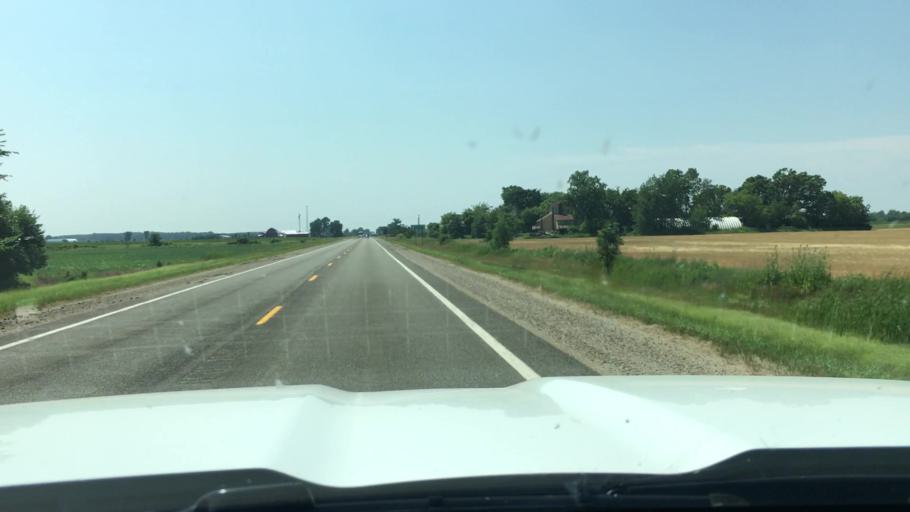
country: US
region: Michigan
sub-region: Gratiot County
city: Ithaca
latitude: 43.1759
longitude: -84.4992
